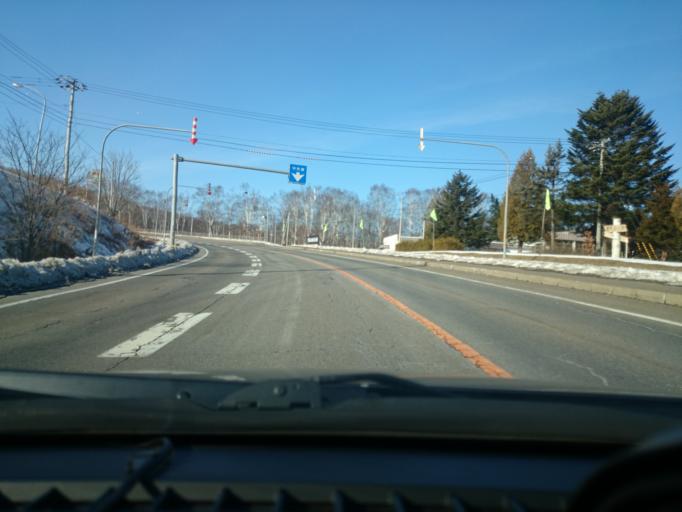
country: JP
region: Hokkaido
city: Otofuke
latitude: 43.2383
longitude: 143.5376
